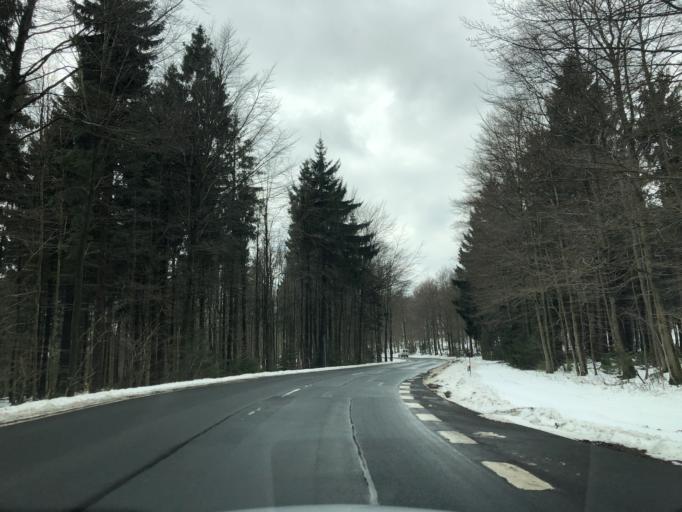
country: DE
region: Hesse
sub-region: Regierungsbezirk Giessen
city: Ulrichstein
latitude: 50.5117
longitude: 9.2333
